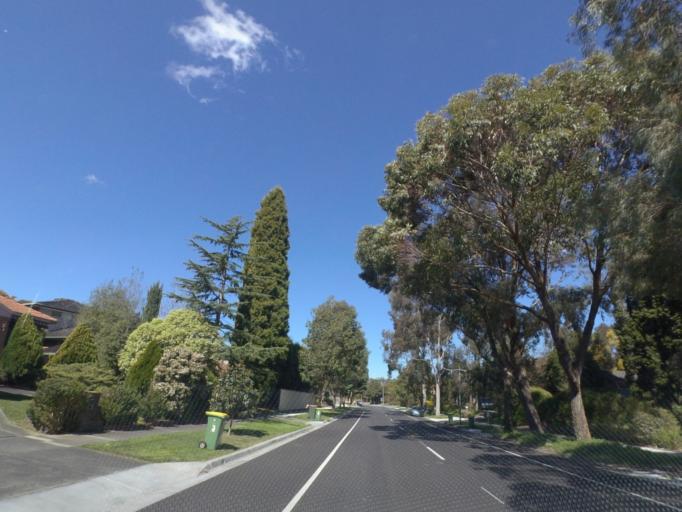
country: AU
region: Victoria
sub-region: Knox
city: Wantirna South
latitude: -37.8701
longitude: 145.2197
